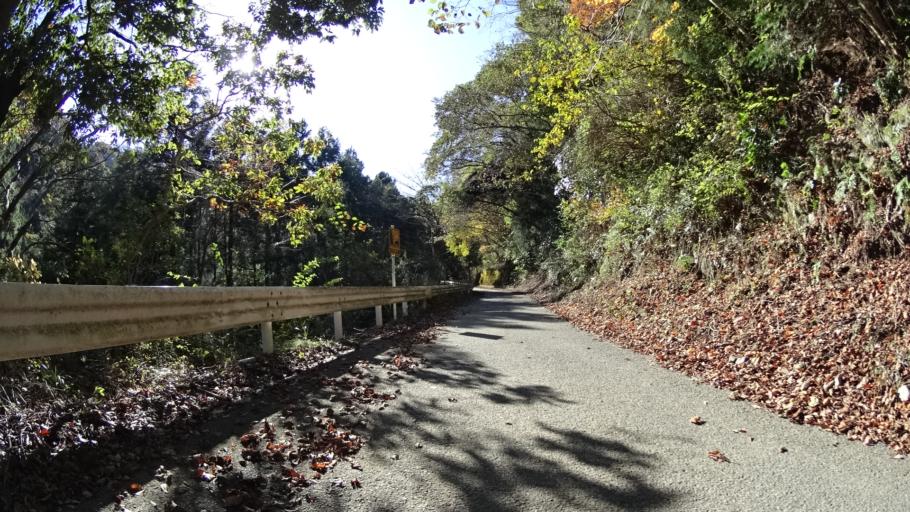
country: JP
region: Kanagawa
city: Atsugi
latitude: 35.5121
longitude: 139.2705
